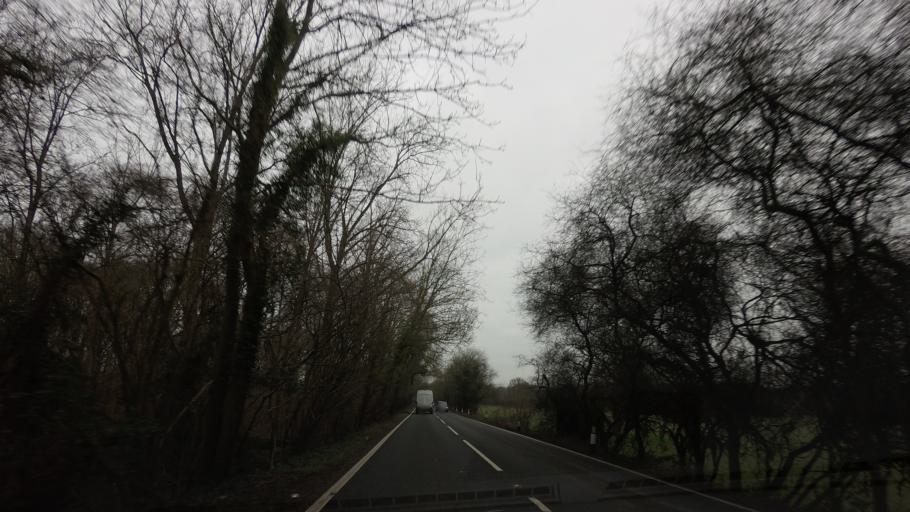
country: GB
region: England
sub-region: Kent
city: Staplehurst
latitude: 51.1307
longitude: 0.5601
